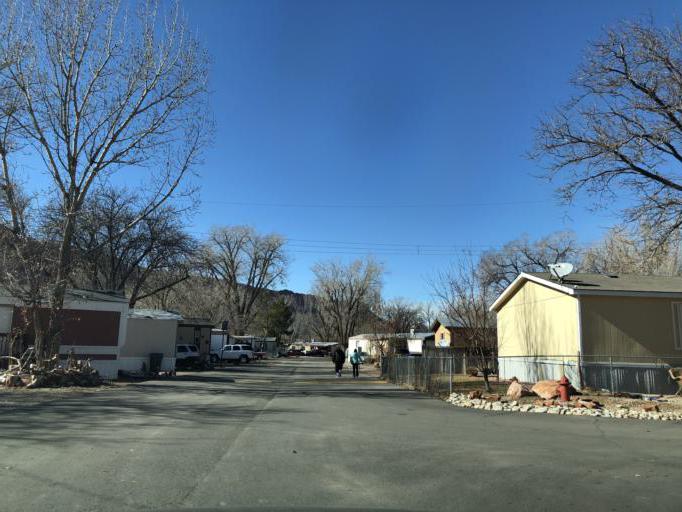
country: US
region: Utah
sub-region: Grand County
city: Moab
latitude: 38.5759
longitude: -109.5640
